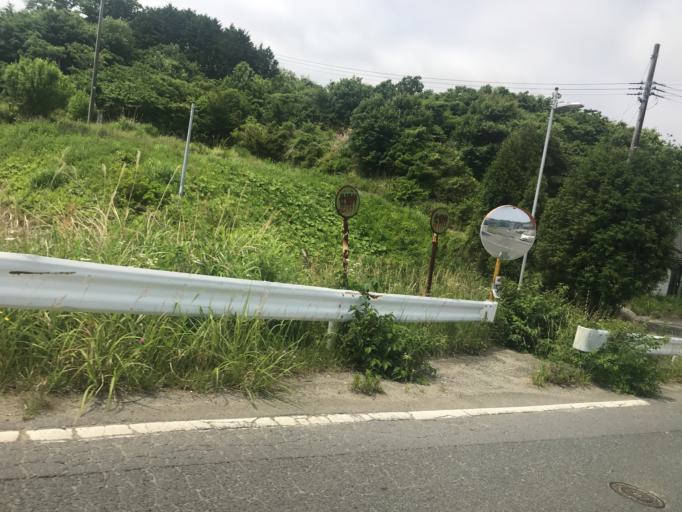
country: JP
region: Fukushima
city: Namie
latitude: 37.2802
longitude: 141.0021
